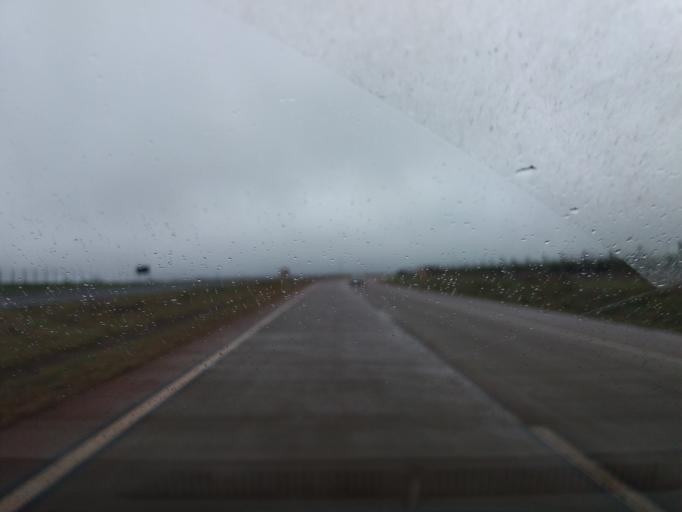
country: BR
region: Parana
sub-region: Cascavel
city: Cascavel
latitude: -25.1306
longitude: -53.5866
